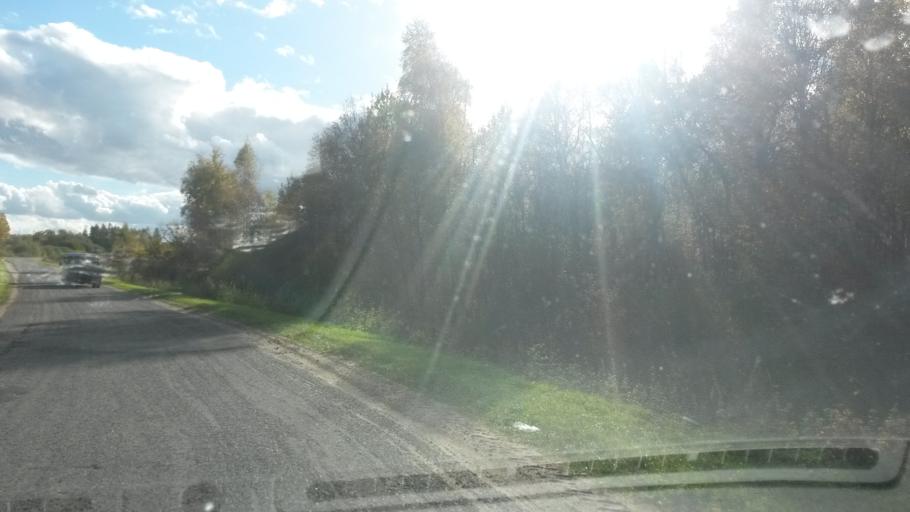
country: RU
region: Jaroslavl
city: Tunoshna
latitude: 57.5282
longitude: 40.0108
